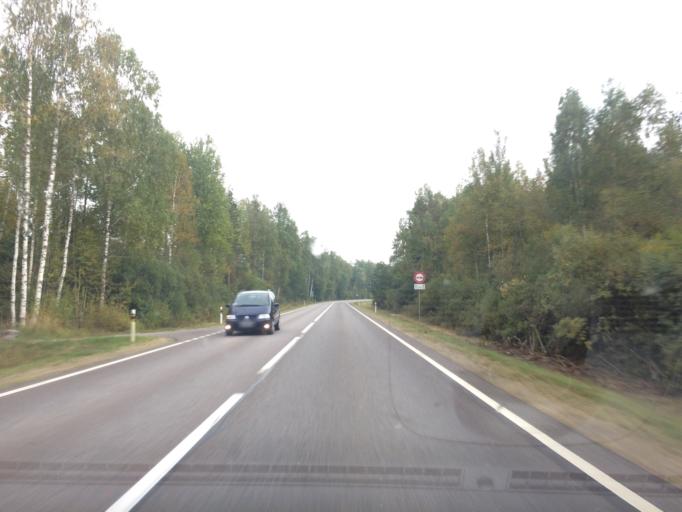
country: LV
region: Livani
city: Livani
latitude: 56.5365
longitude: 26.1355
